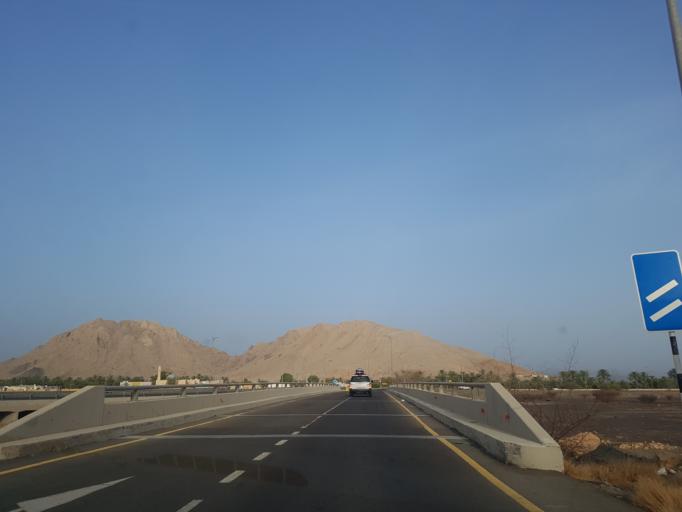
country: OM
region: Al Buraimi
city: Al Buraymi
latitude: 24.2308
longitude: 55.9551
